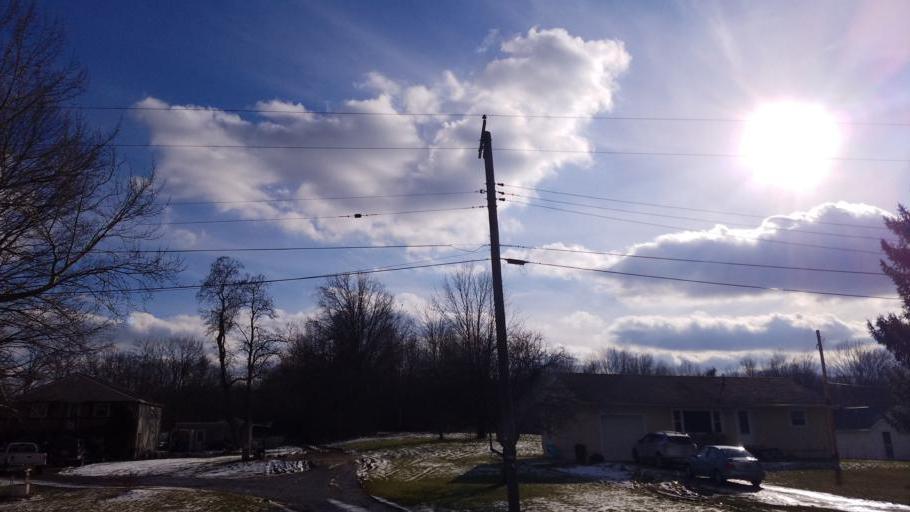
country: US
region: Ohio
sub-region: Richland County
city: Ontario
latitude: 40.7790
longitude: -82.6422
